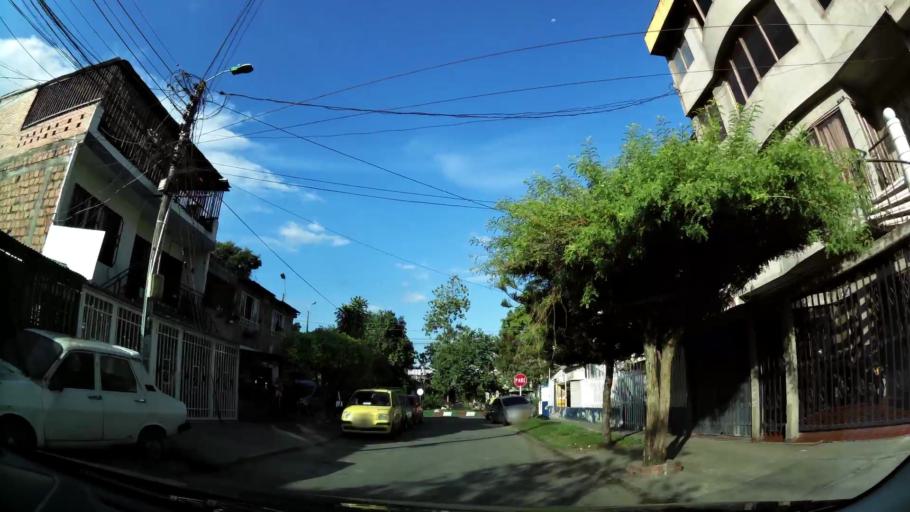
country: CO
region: Valle del Cauca
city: Cali
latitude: 3.4151
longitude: -76.5109
